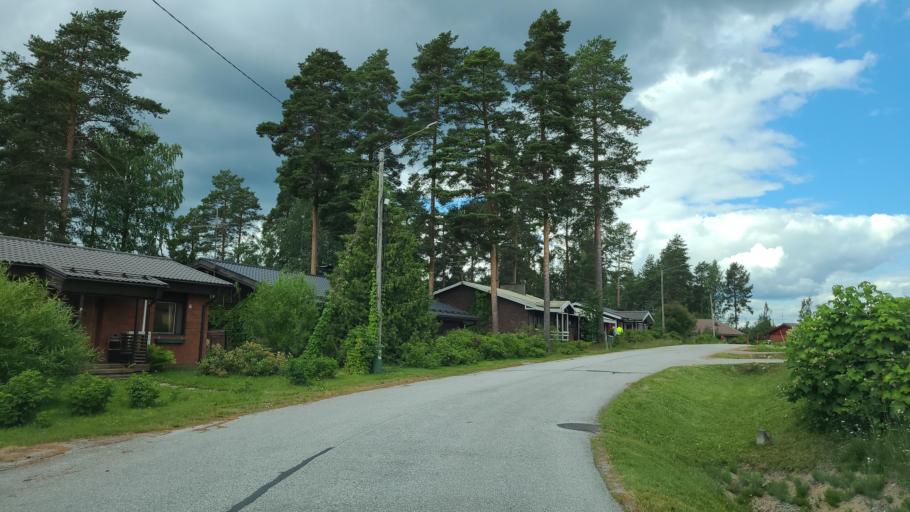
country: FI
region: Northern Savo
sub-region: Koillis-Savo
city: Kaavi
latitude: 62.9734
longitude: 28.4730
